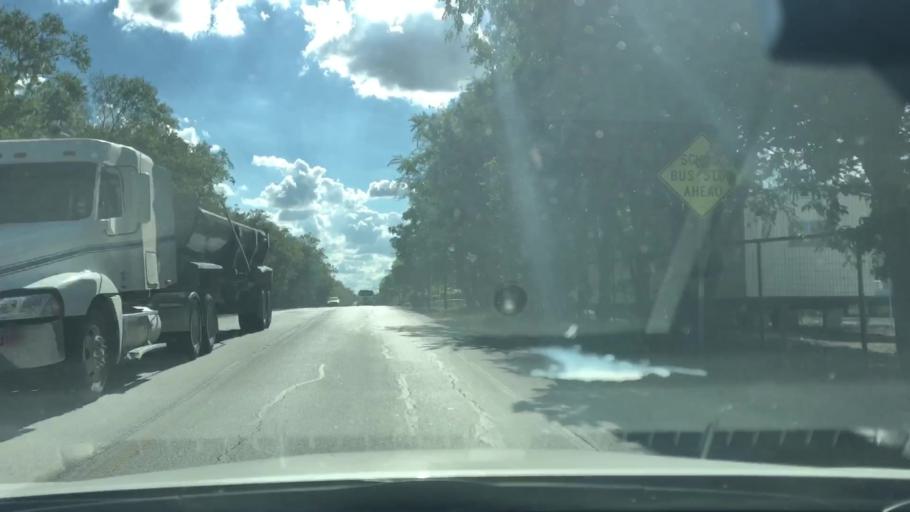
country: US
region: Texas
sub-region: Comal County
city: New Braunfels
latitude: 29.6648
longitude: -98.1745
